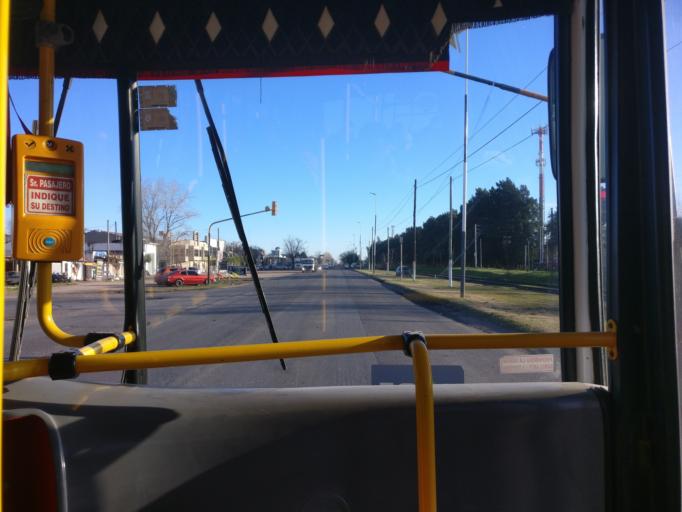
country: AR
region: Buenos Aires
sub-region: Partido de Ezeiza
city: Ezeiza
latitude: -34.8973
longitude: -58.5777
